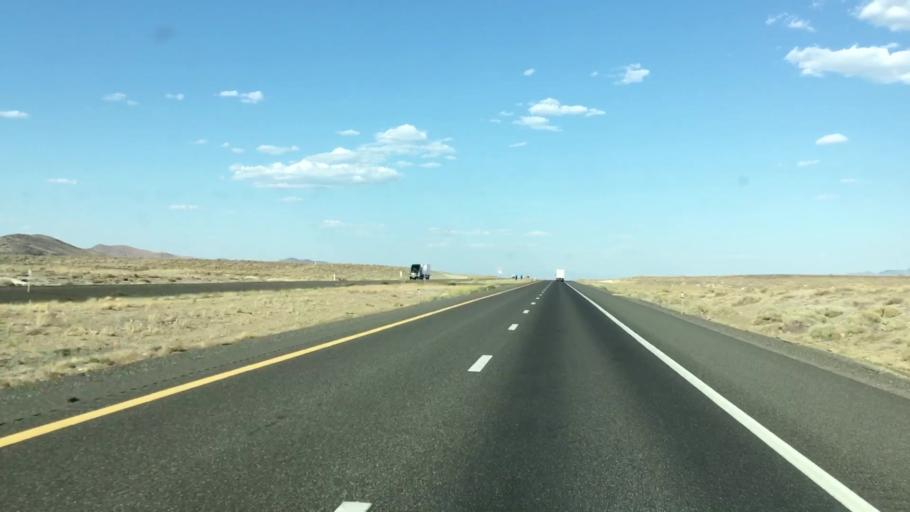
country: US
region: Nevada
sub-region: Churchill County
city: Fallon
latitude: 39.8578
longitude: -118.9154
